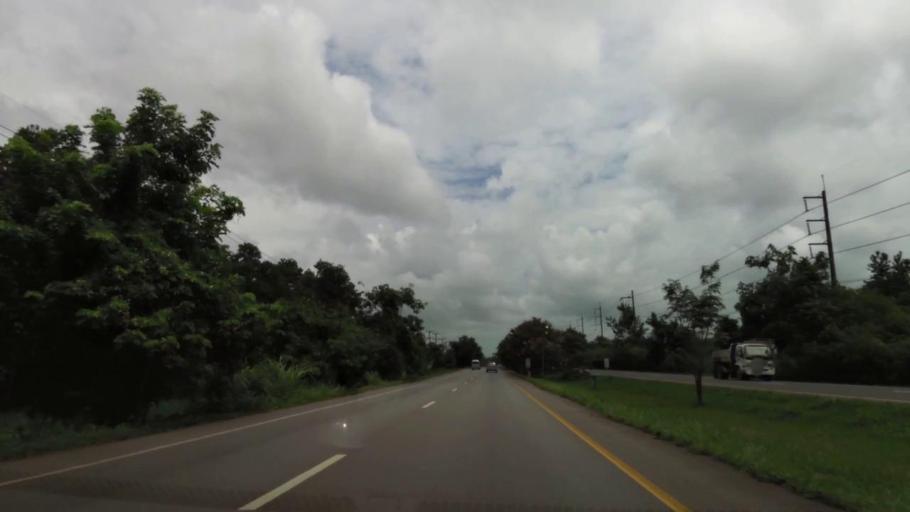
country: TH
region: Chanthaburi
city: Na Yai Am
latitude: 12.7484
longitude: 101.8763
